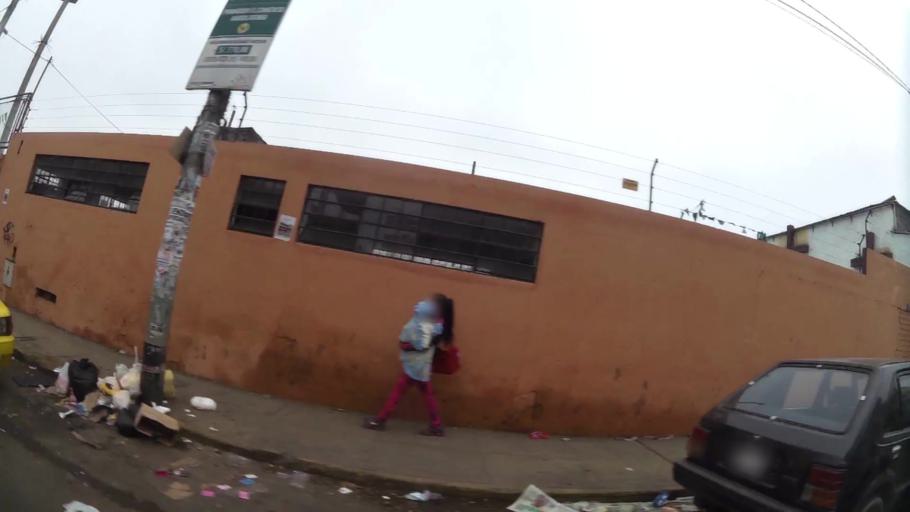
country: PE
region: Lima
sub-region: Lima
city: Surco
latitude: -12.1509
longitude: -76.9701
